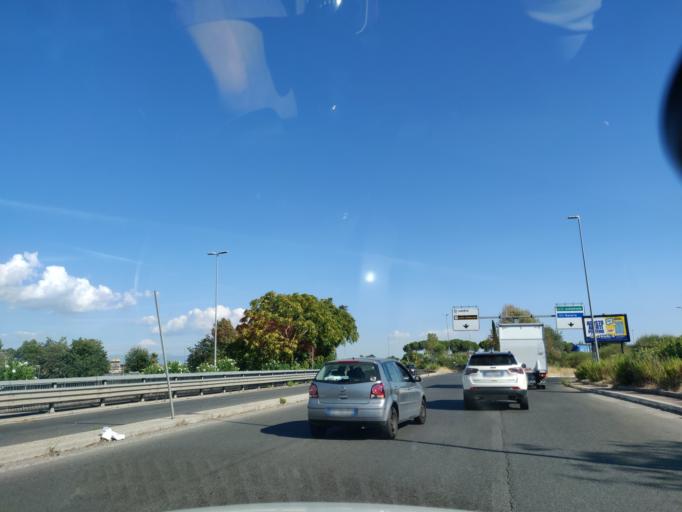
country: IT
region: Latium
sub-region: Citta metropolitana di Roma Capitale
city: Colle Verde
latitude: 41.9691
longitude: 12.5384
